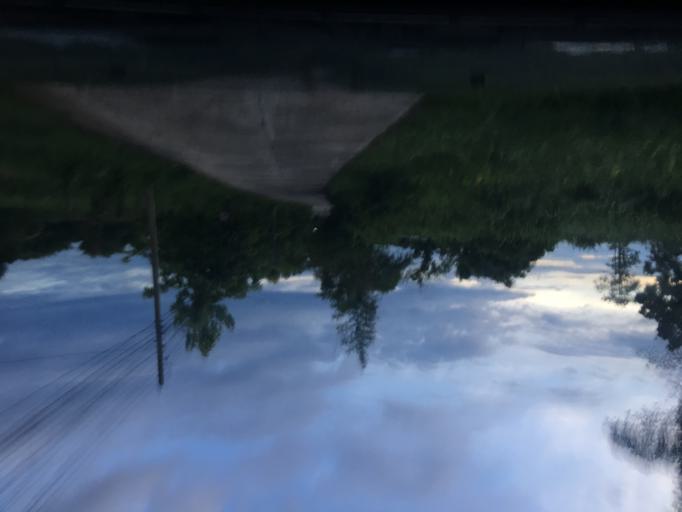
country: TH
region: Chiang Mai
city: San Sai
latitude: 18.8700
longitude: 98.9675
